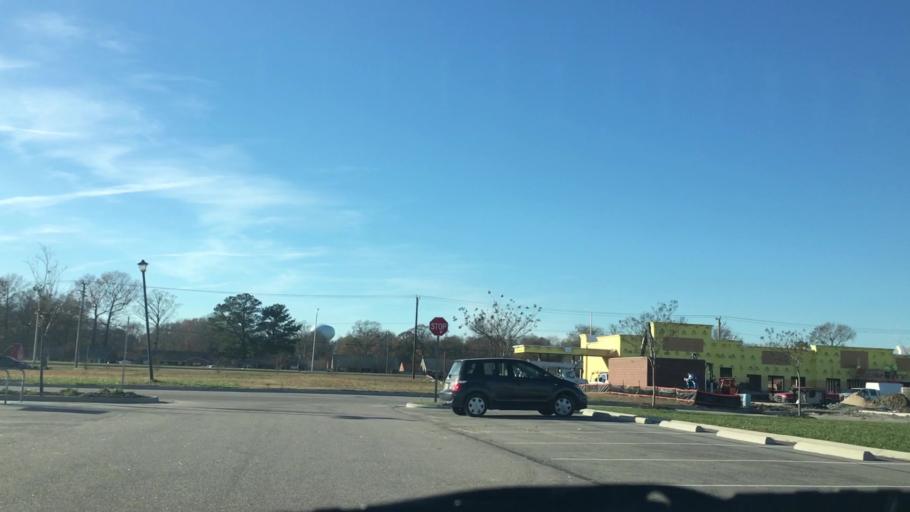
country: US
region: Virginia
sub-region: City of Portsmouth
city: Portsmouth Heights
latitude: 36.8728
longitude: -76.4219
